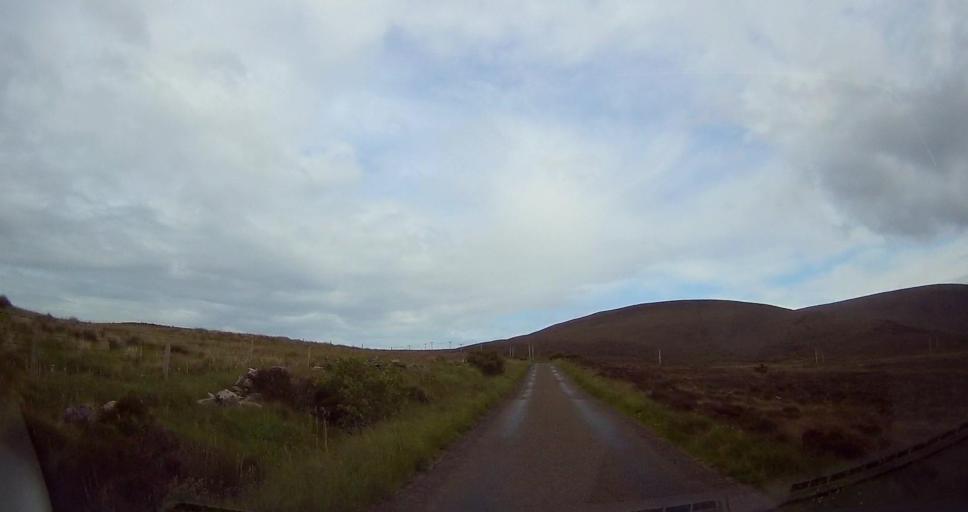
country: GB
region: Scotland
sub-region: Orkney Islands
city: Stromness
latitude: 58.9038
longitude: -3.3071
